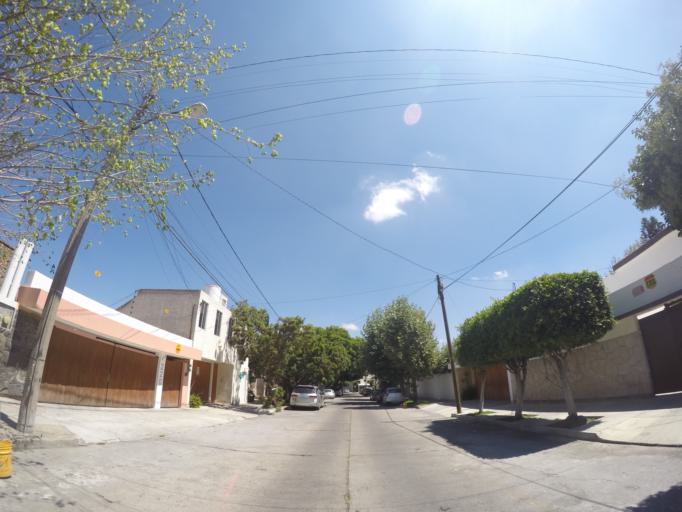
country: MX
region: San Luis Potosi
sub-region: San Luis Potosi
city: San Luis Potosi
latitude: 22.1468
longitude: -101.0049
